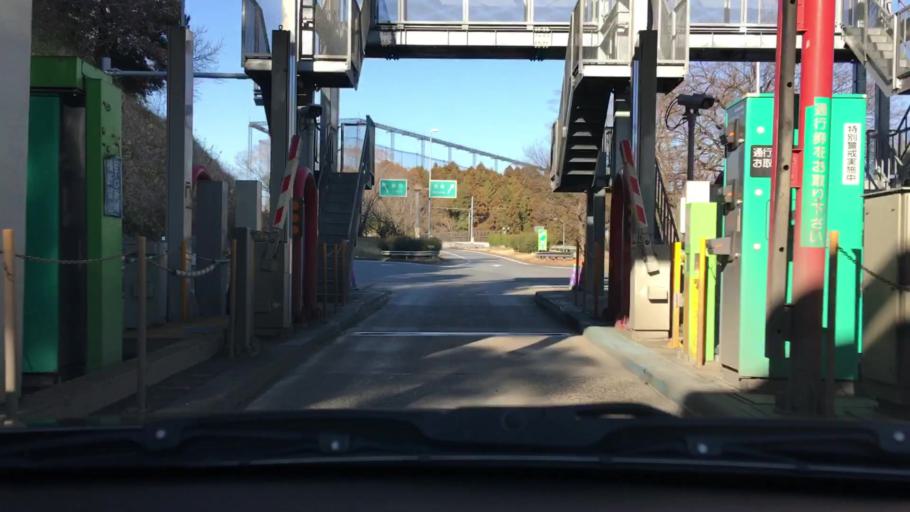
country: JP
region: Chiba
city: Sakura
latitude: 35.6858
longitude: 140.2378
